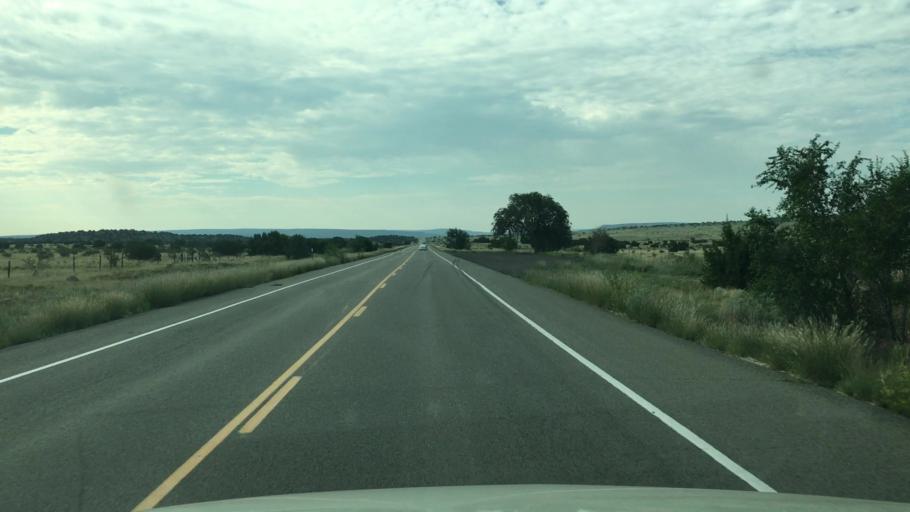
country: US
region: New Mexico
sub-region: Santa Fe County
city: Eldorado at Santa Fe
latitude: 35.4491
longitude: -105.8896
